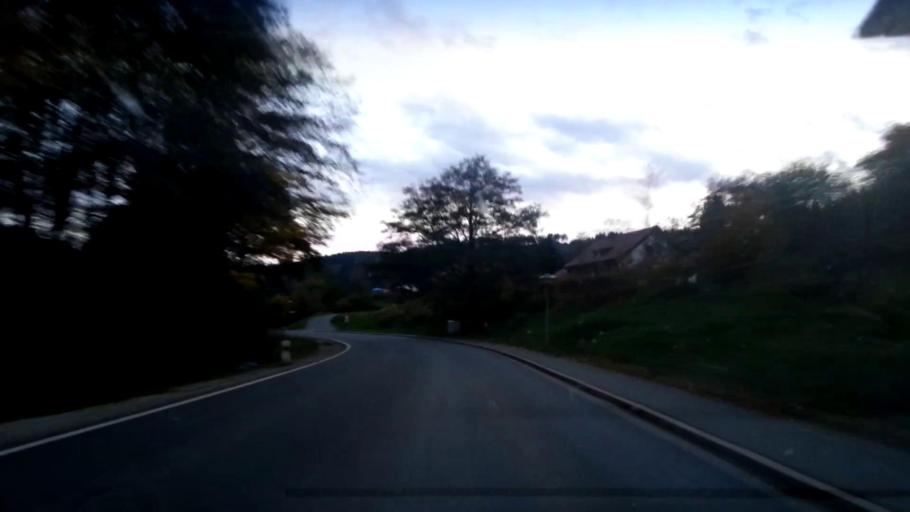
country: DE
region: Bavaria
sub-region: Upper Franconia
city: Warmensteinach
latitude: 49.9896
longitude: 11.7746
